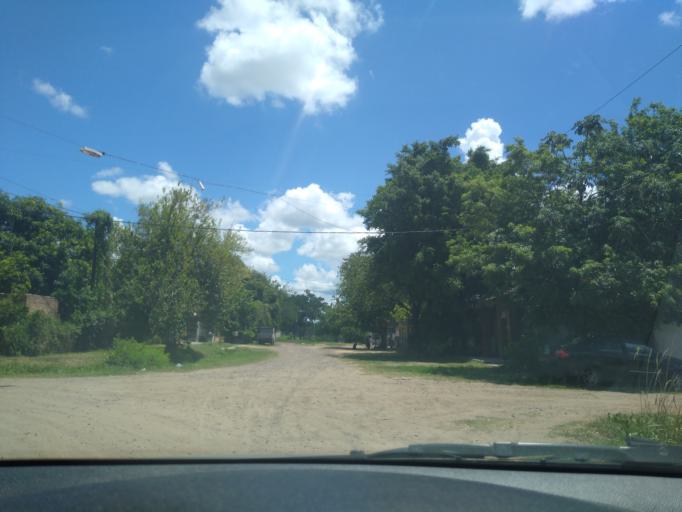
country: AR
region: Chaco
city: Barranqueras
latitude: -27.4787
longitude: -58.9368
